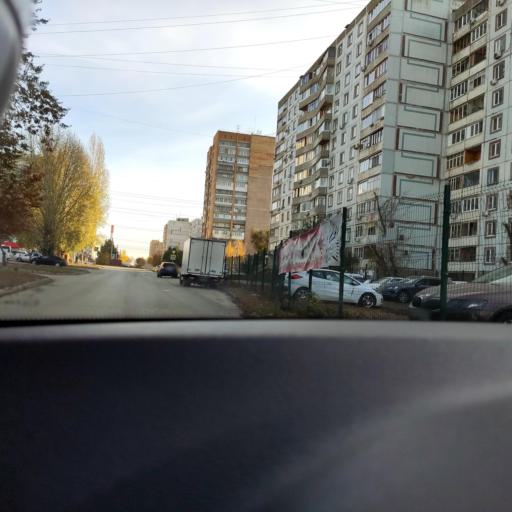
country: RU
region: Samara
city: Samara
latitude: 53.1998
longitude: 50.1430
